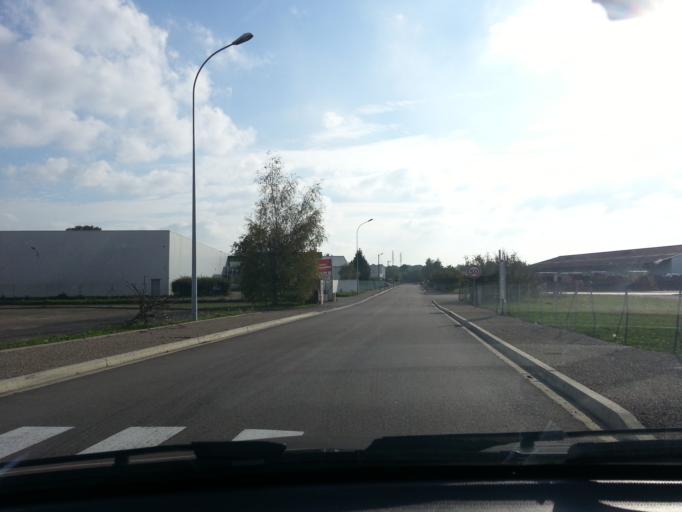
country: FR
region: Bourgogne
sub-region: Departement de Saone-et-Loire
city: Chatenoy-le-Royal
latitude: 46.7995
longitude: 4.7941
